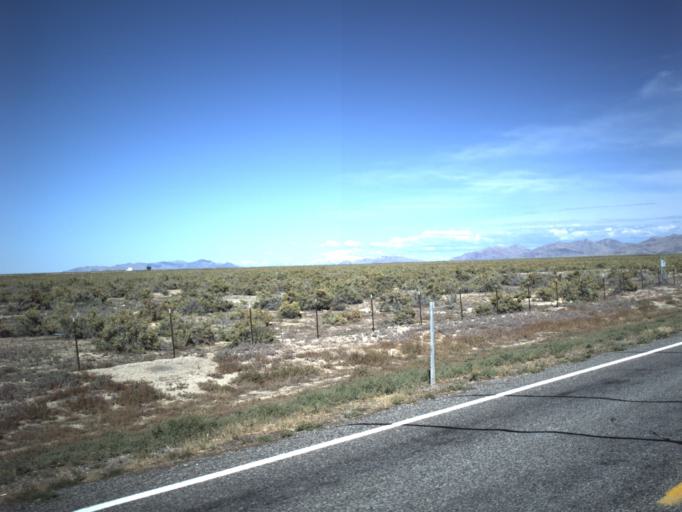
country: US
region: Utah
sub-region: Millard County
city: Delta
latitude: 39.3530
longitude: -112.5259
